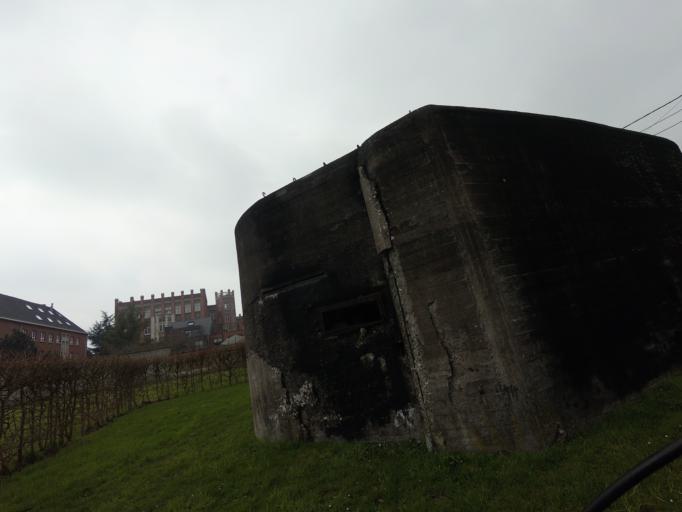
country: BE
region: Flanders
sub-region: Provincie Antwerpen
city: Sint-Katelijne-Waver
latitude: 51.0649
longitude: 4.5813
